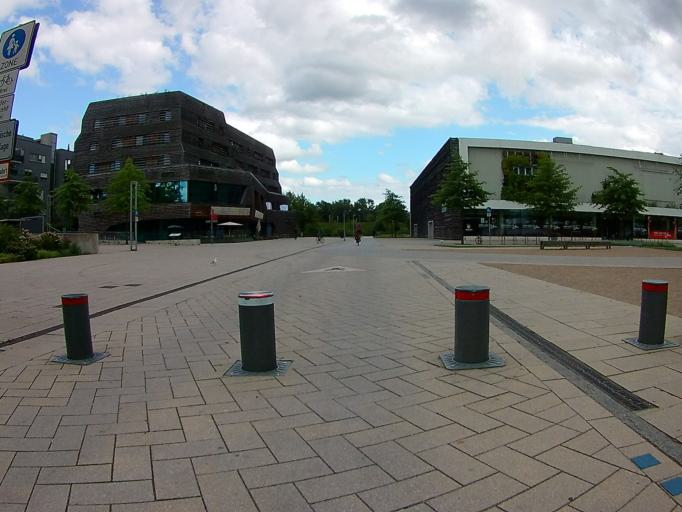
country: DE
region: Hamburg
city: Kleiner Grasbrook
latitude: 53.4964
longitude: 10.0018
